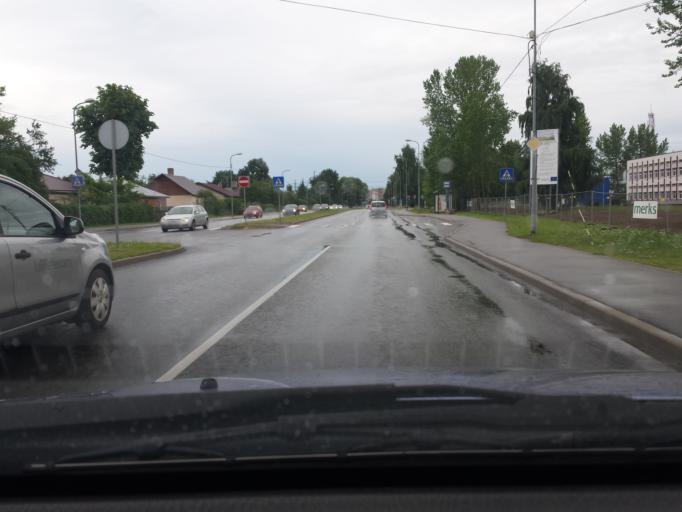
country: LV
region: Riga
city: Riga
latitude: 56.9379
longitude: 24.1821
